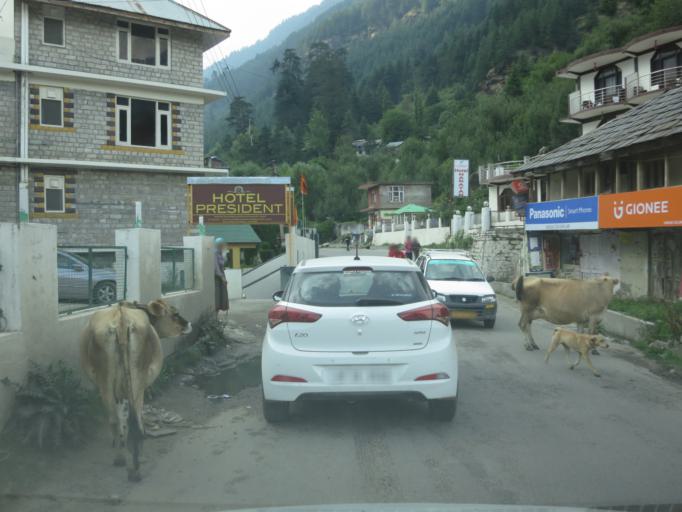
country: IN
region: Himachal Pradesh
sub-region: Kulu
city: Manali
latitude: 32.2315
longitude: 77.1967
